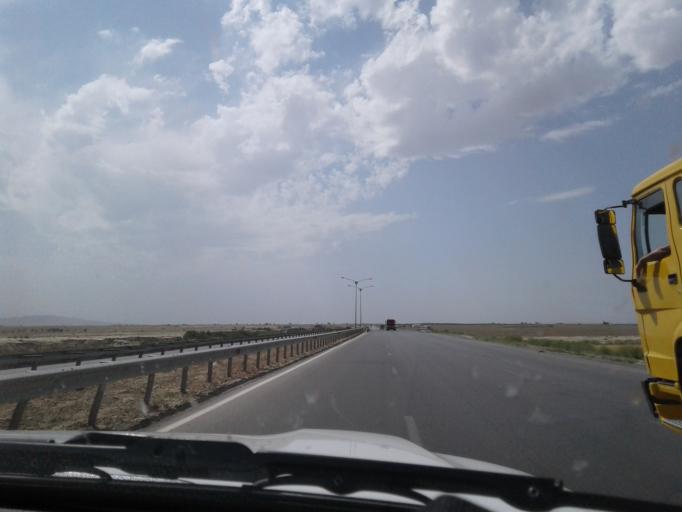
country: TM
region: Ahal
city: Annau
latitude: 37.8010
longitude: 58.8007
